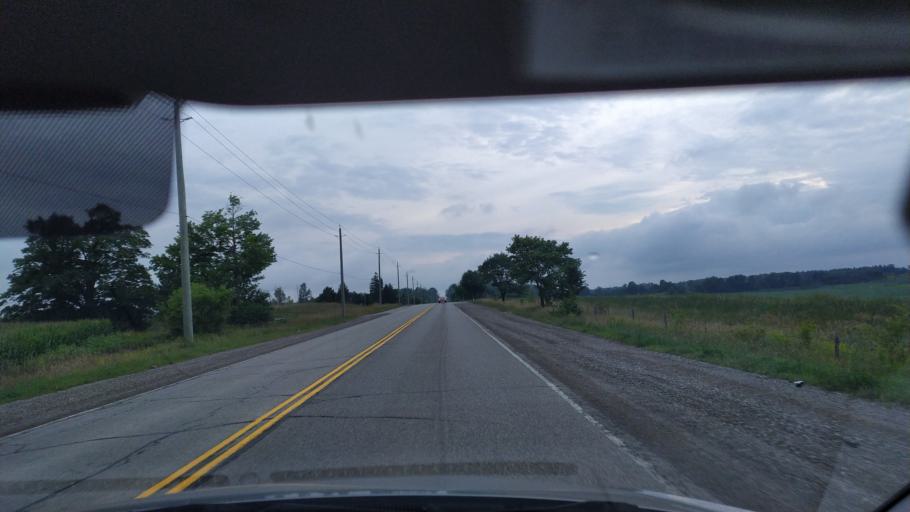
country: CA
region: Ontario
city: Cambridge
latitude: 43.3485
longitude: -80.3470
